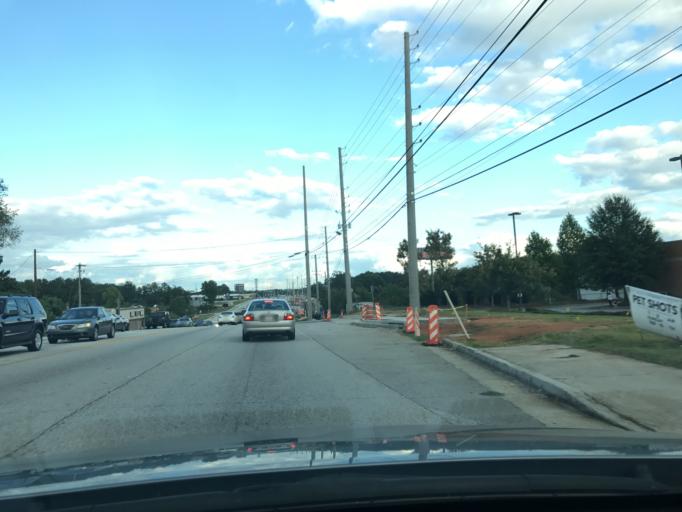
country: US
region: Georgia
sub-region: Douglas County
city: Douglasville
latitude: 33.7511
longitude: -84.7264
